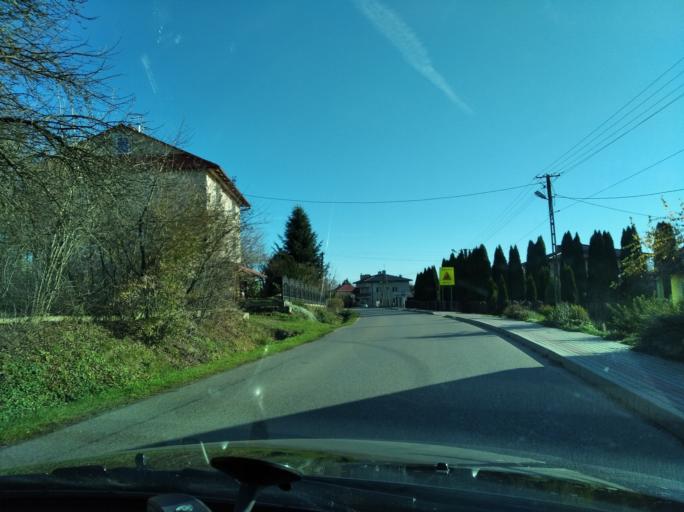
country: PL
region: Subcarpathian Voivodeship
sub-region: Powiat rzeszowski
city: Lutoryz
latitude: 49.9649
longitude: 21.9158
